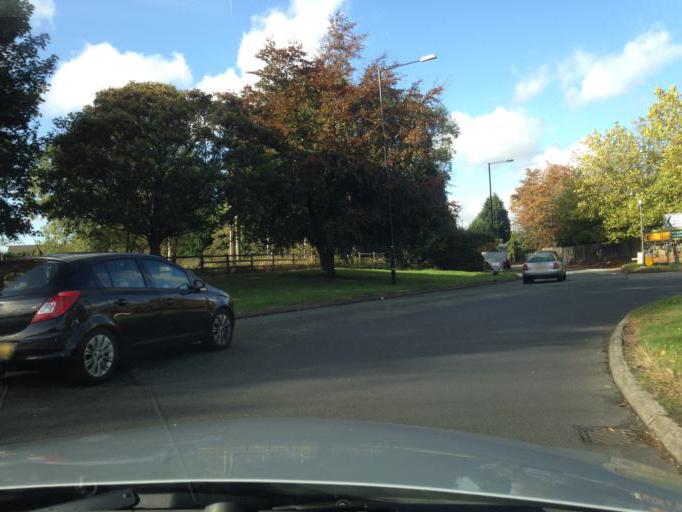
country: GB
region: England
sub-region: Manchester
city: Ringway
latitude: 53.3630
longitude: -2.2981
